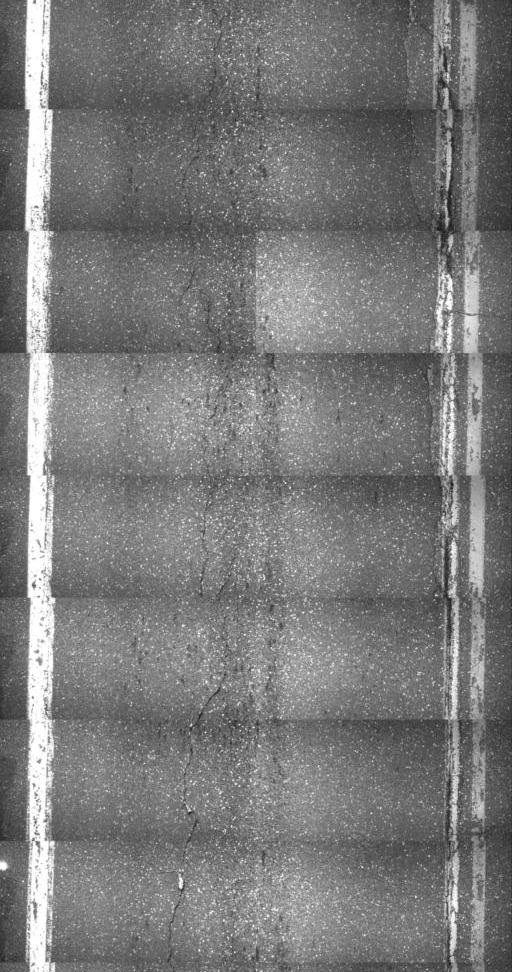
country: US
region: Vermont
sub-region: Windsor County
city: Woodstock
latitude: 43.5096
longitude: -72.5524
